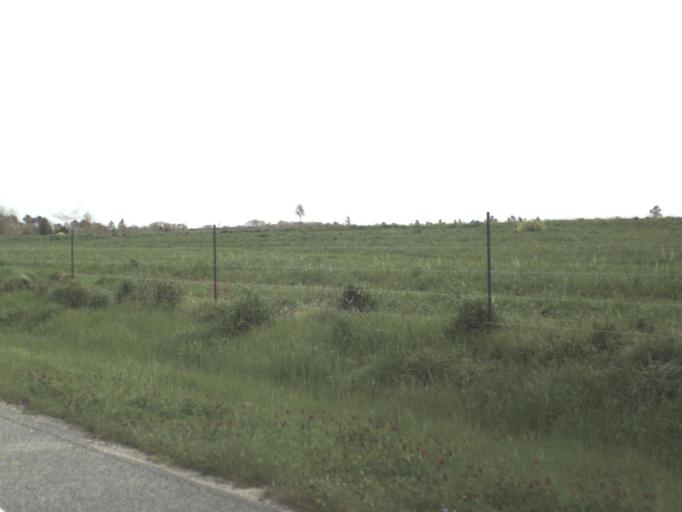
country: US
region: Florida
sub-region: Jackson County
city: Graceville
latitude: 30.9559
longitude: -85.6482
